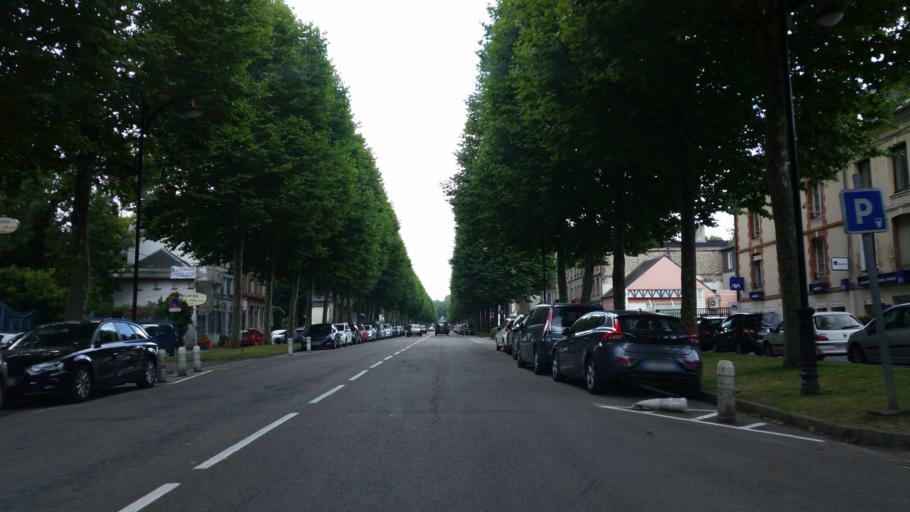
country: FR
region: Lower Normandy
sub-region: Departement du Calvados
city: Honfleur
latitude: 49.4161
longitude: 0.2300
